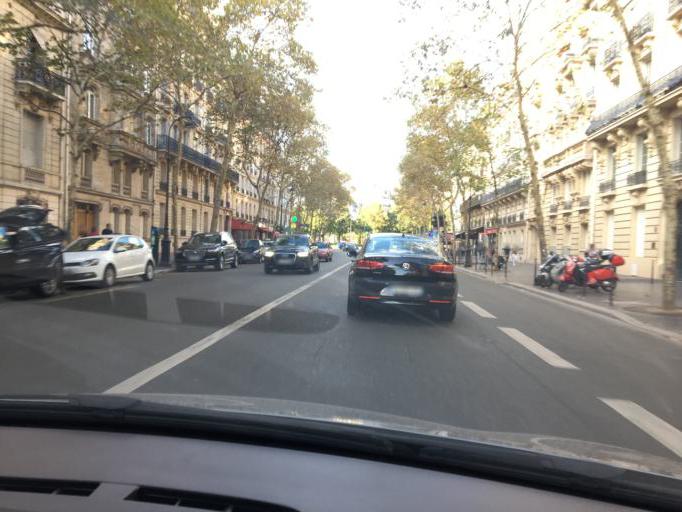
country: FR
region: Ile-de-France
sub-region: Departement des Hauts-de-Seine
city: Levallois-Perret
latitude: 48.8834
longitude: 2.2967
